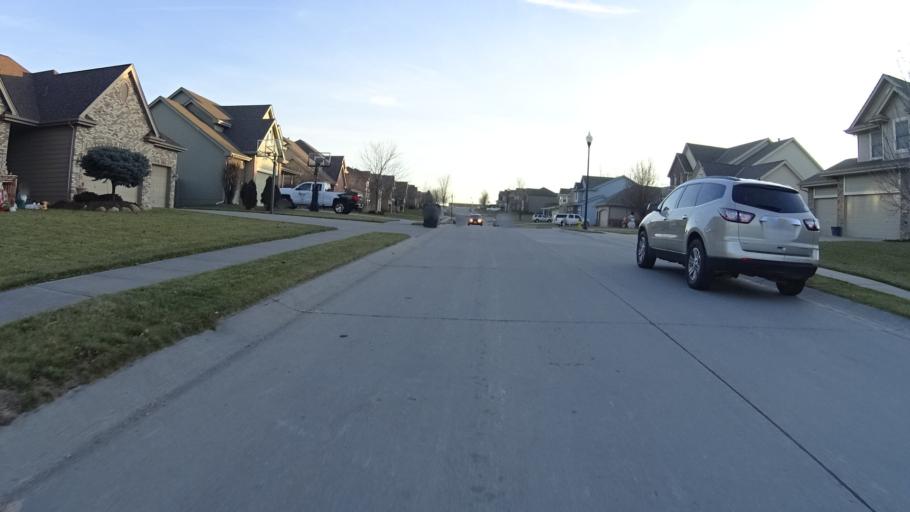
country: US
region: Nebraska
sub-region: Sarpy County
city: Papillion
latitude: 41.1300
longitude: -96.0673
